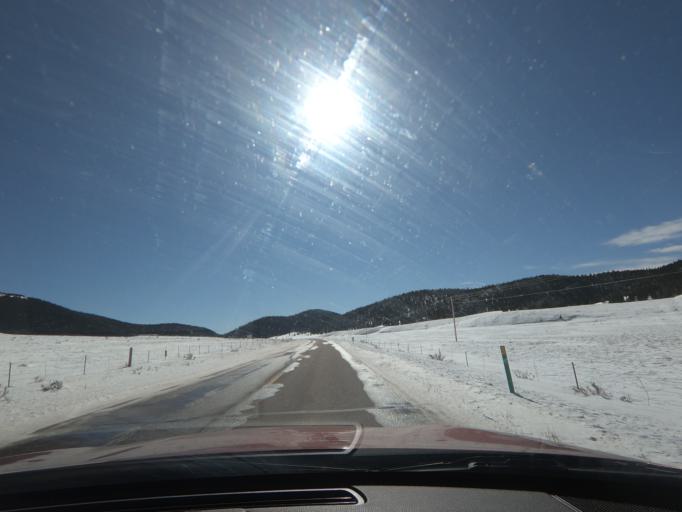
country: US
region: Colorado
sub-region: Teller County
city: Cripple Creek
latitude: 38.7667
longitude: -105.1175
